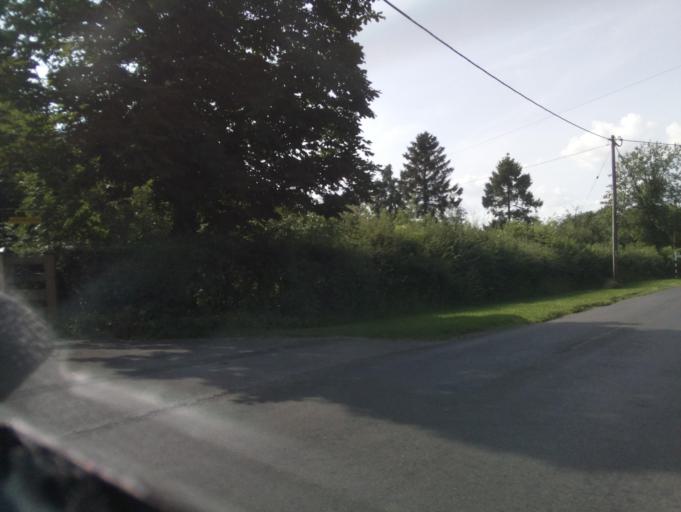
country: GB
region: England
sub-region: Wiltshire
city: Minety
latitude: 51.6209
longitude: -1.9669
